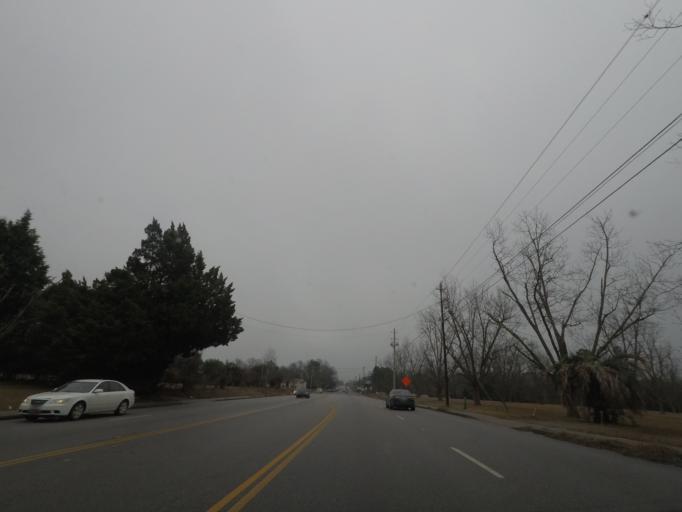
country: US
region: South Carolina
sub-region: Clarendon County
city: Manning
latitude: 33.6994
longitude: -80.2353
